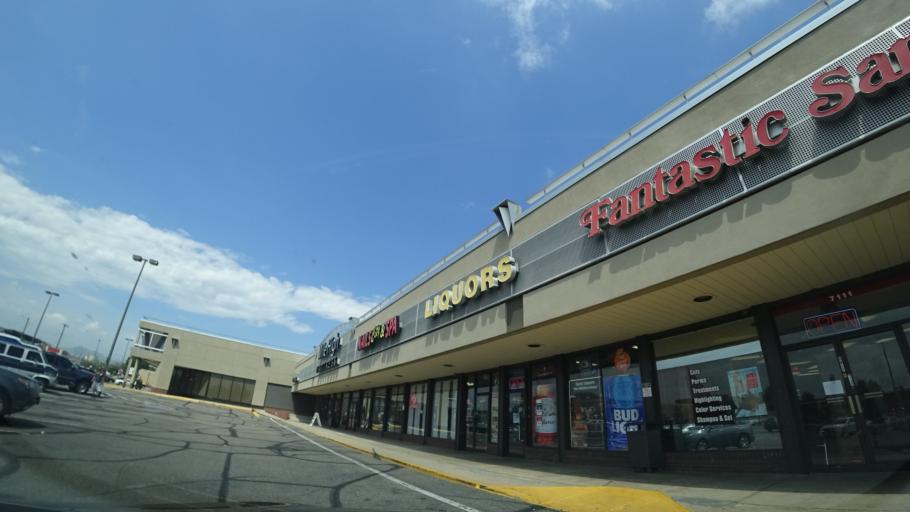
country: US
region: Colorado
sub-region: Jefferson County
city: Lakewood
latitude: 39.7118
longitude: -105.0752
